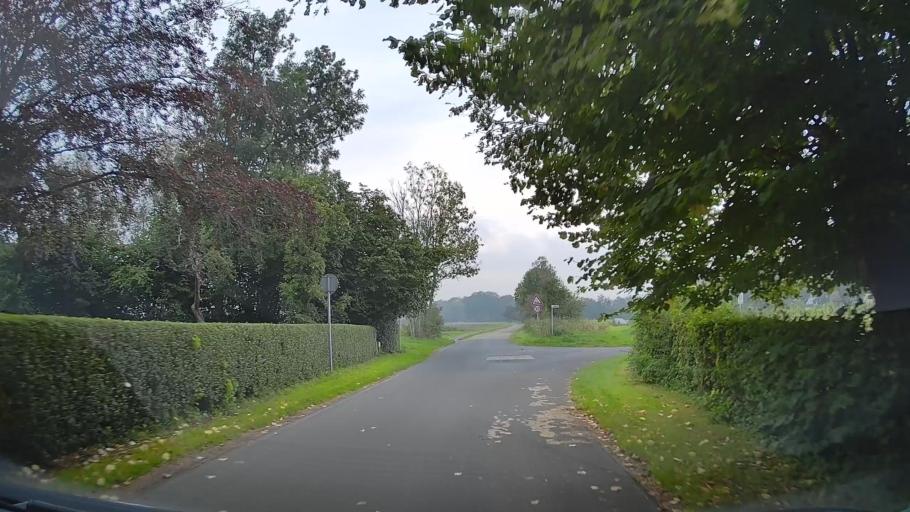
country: DE
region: Lower Saxony
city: Cuxhaven
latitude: 53.8323
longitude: 8.7600
